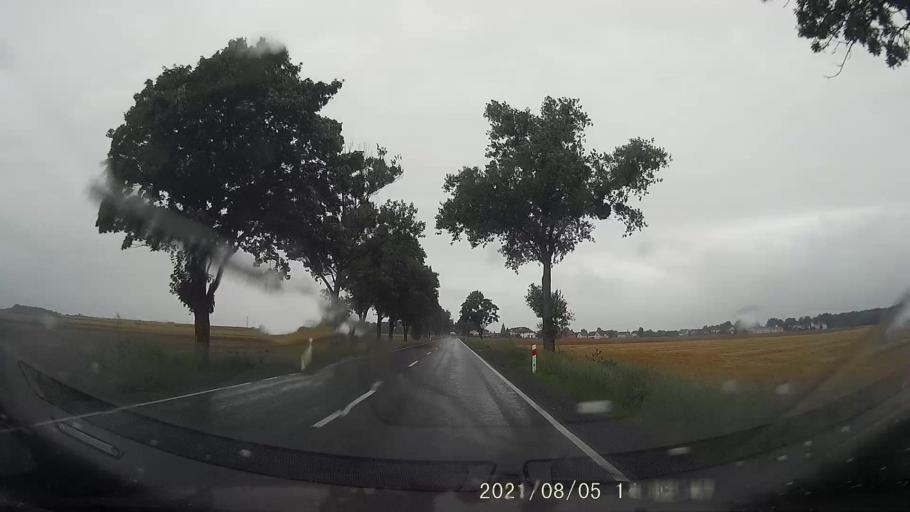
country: PL
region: Opole Voivodeship
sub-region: Powiat krapkowicki
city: Strzeleczki
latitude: 50.4567
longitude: 17.8677
